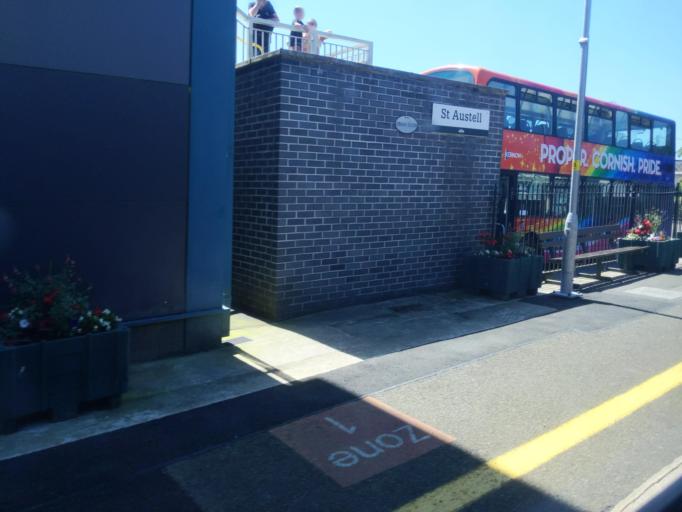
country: GB
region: England
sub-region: Cornwall
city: St Austell
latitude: 50.3396
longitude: -4.7895
